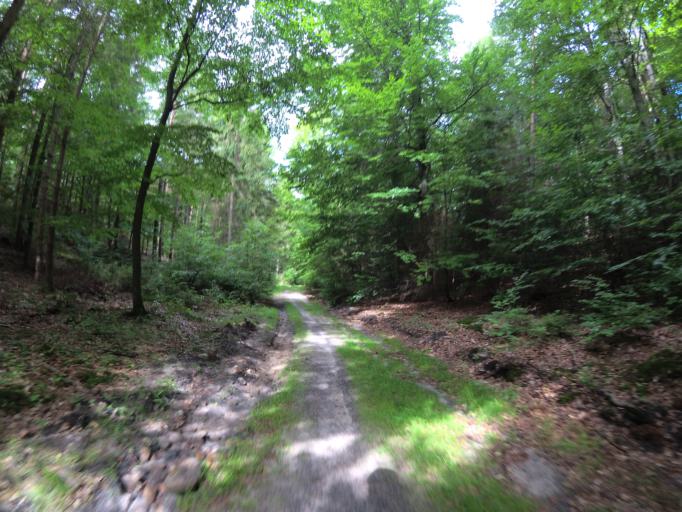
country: PL
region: Pomeranian Voivodeship
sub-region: Gdynia
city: Wielki Kack
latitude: 54.5066
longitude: 18.4446
